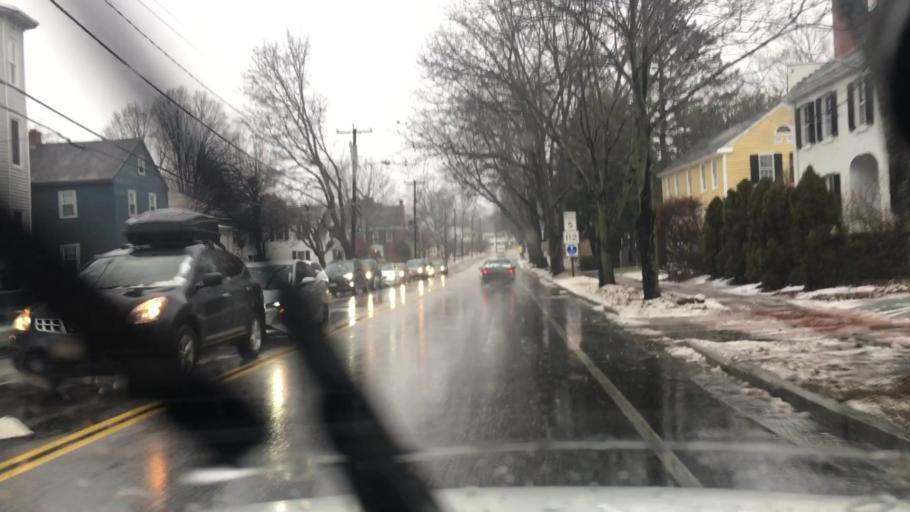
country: US
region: Maine
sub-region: York County
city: Saco
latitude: 43.5013
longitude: -70.4435
